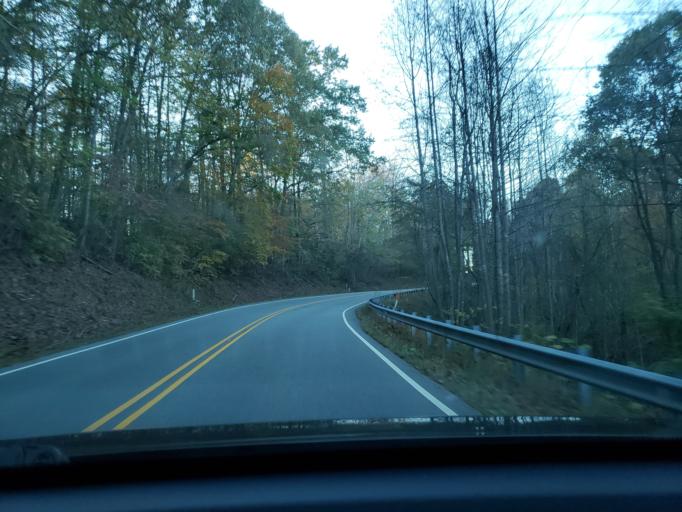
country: US
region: North Carolina
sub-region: Stokes County
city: Danbury
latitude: 36.3939
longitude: -80.1967
